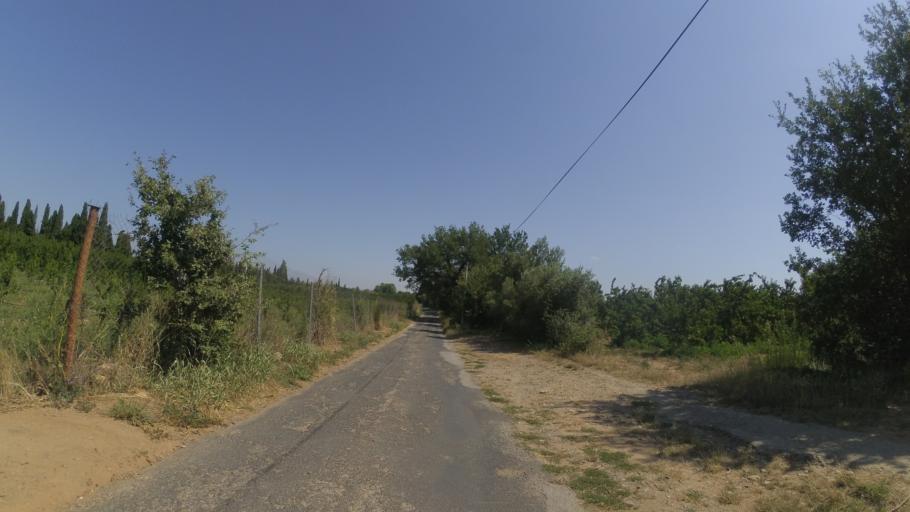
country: FR
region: Languedoc-Roussillon
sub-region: Departement des Pyrenees-Orientales
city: Corneilla-la-Riviere
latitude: 42.6641
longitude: 2.7251
